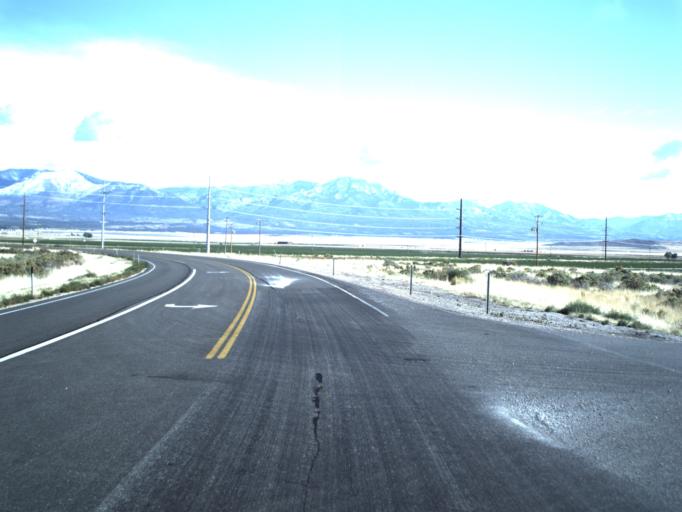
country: US
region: Utah
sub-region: Millard County
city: Fillmore
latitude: 39.1193
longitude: -112.3555
